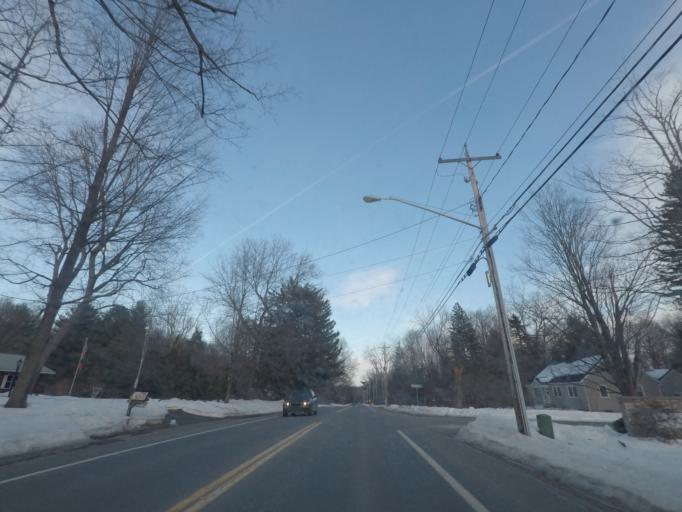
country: US
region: New York
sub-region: Schenectady County
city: Niskayuna
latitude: 42.8372
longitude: -73.8180
